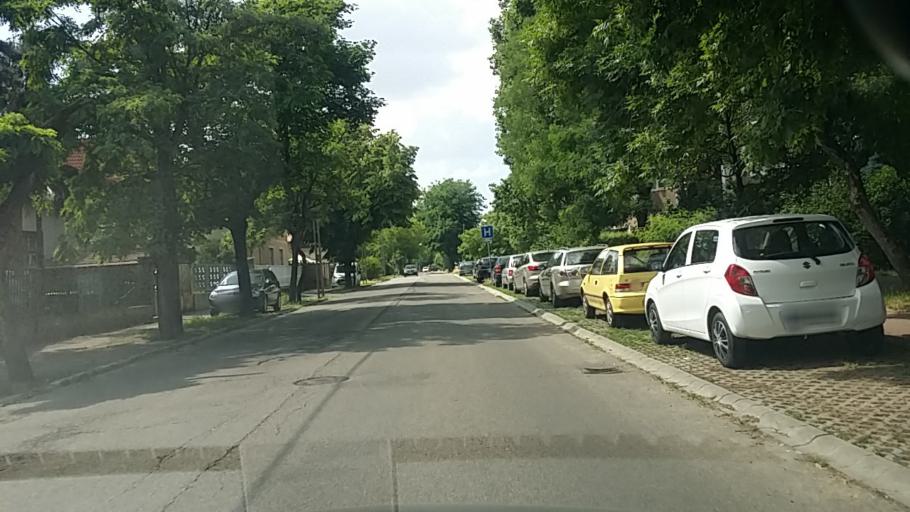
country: HU
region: Budapest
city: Budapest XV. keruelet
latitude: 47.5596
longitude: 19.1065
